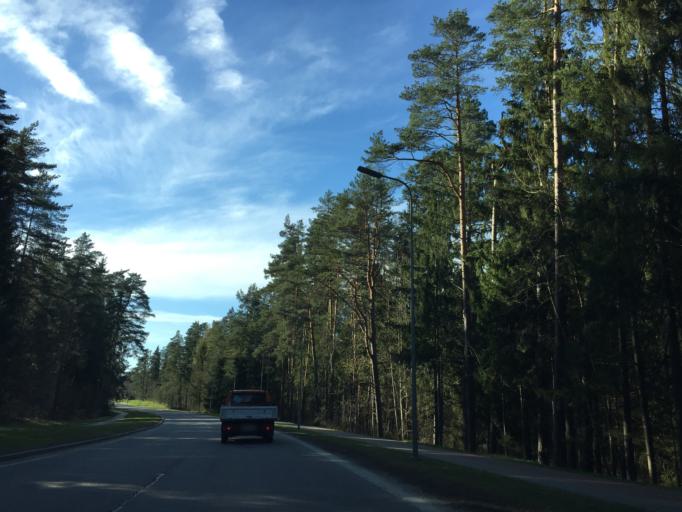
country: LV
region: Valkas Rajons
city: Valka
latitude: 57.7845
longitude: 26.0016
